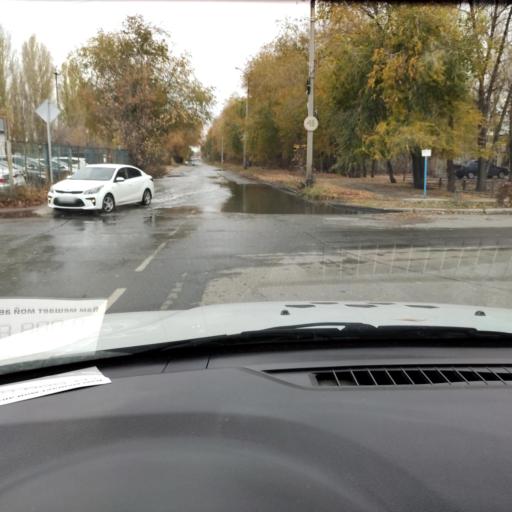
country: RU
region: Samara
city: Tol'yatti
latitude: 53.5519
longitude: 49.3084
